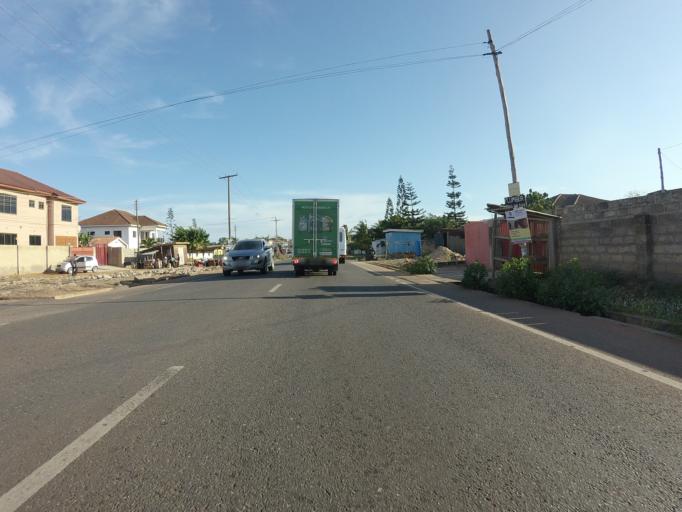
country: GH
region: Greater Accra
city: Nungua
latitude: 5.6419
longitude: -0.0925
